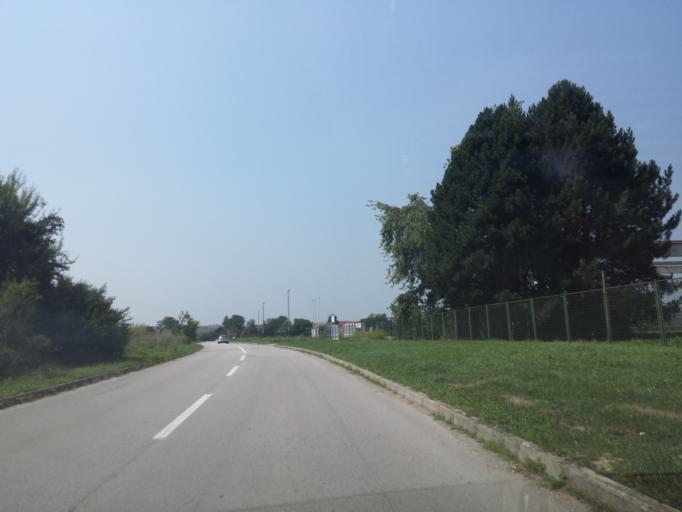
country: HR
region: Zagrebacka
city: Jastrebarsko
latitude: 45.6546
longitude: 15.6503
